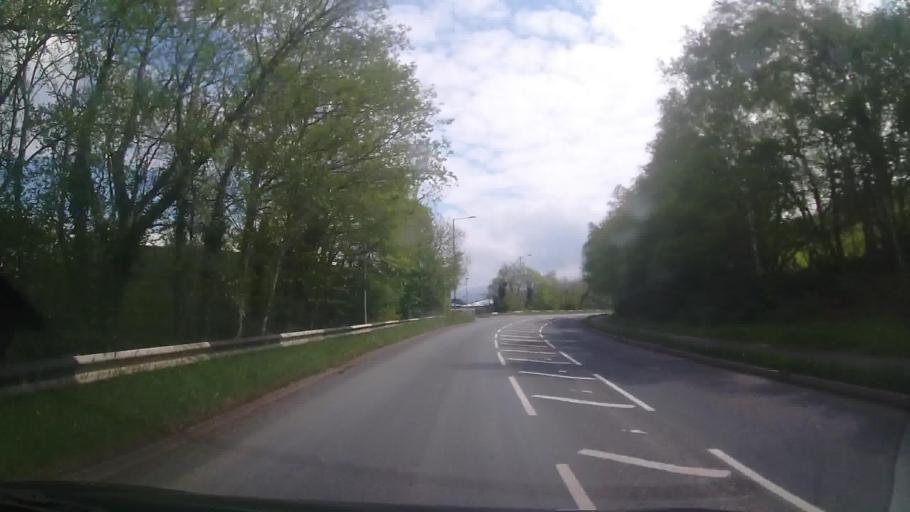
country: GB
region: Wales
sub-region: Gwynedd
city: Porthmadog
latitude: 52.9317
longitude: -4.1477
